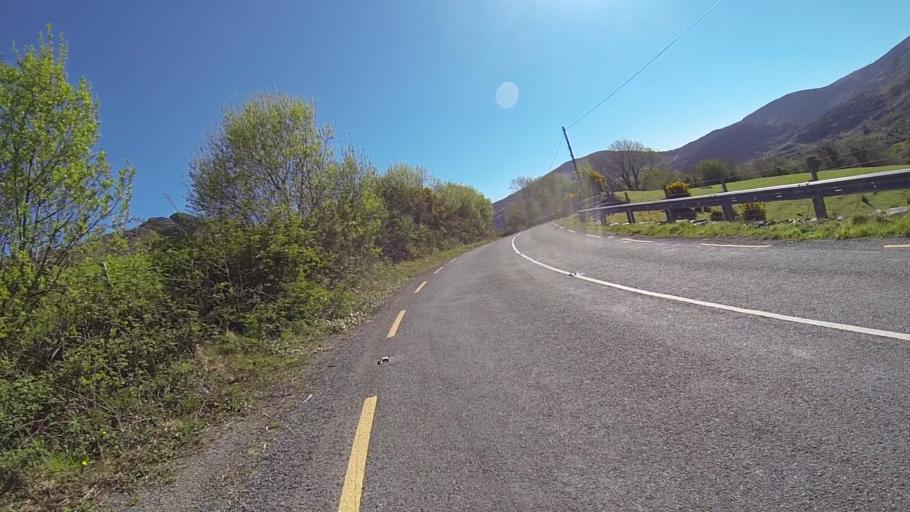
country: IE
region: Munster
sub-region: Ciarrai
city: Kenmare
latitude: 51.7720
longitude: -9.7509
